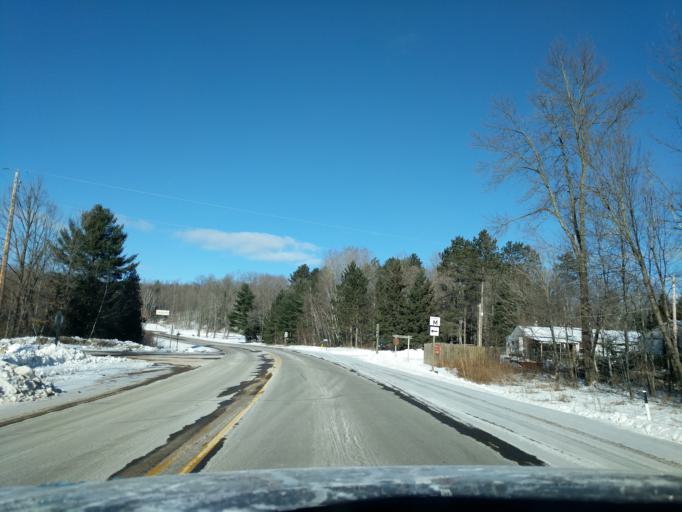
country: US
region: Wisconsin
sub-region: Menominee County
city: Keshena
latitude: 45.1258
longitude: -88.6621
